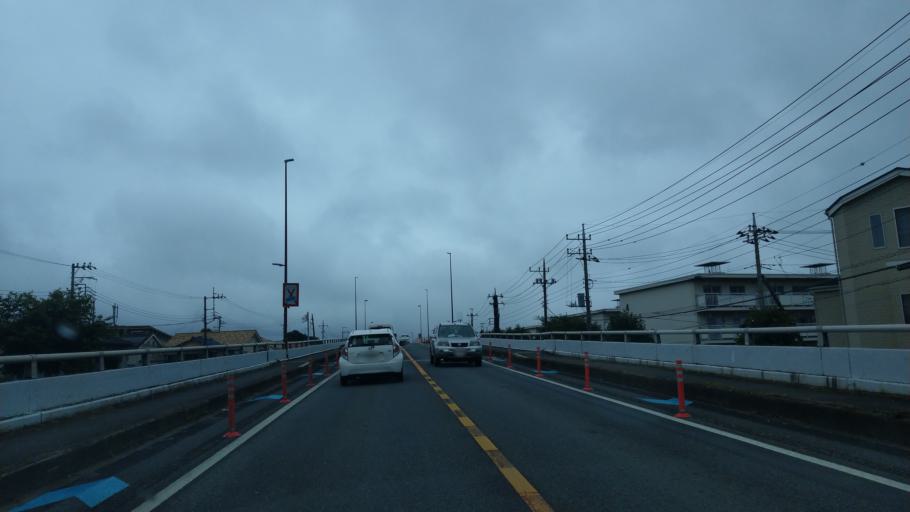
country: JP
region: Saitama
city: Saitama
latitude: 35.9231
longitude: 139.6350
